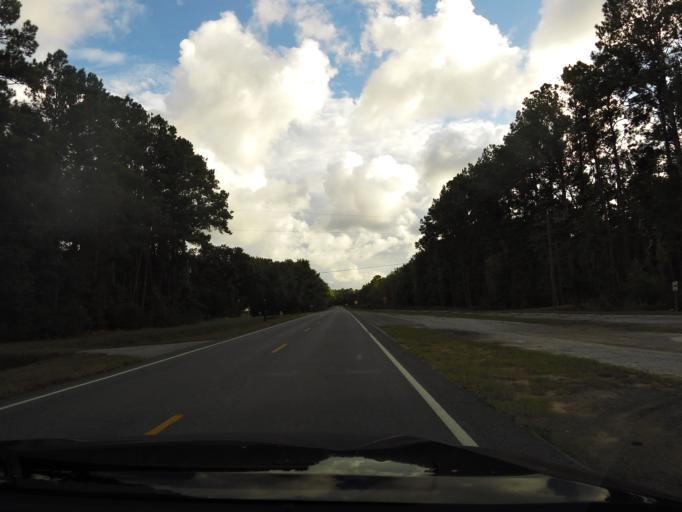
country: US
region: Georgia
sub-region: Liberty County
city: Midway
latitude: 31.7152
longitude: -81.4167
